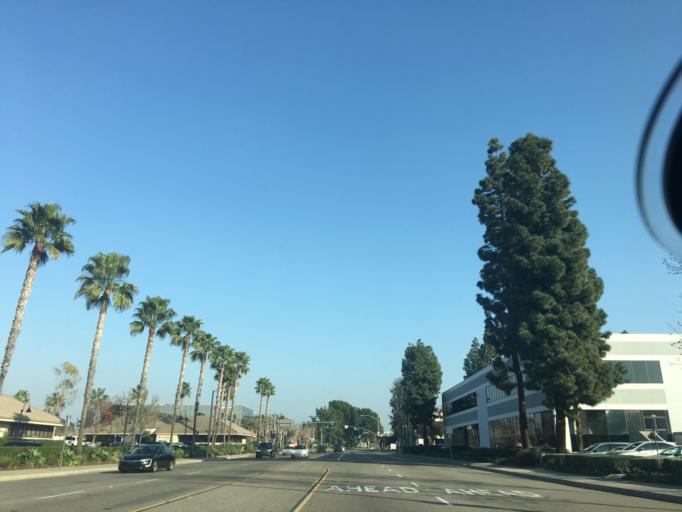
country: US
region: California
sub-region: Orange County
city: Orange
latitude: 33.7956
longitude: -117.8755
